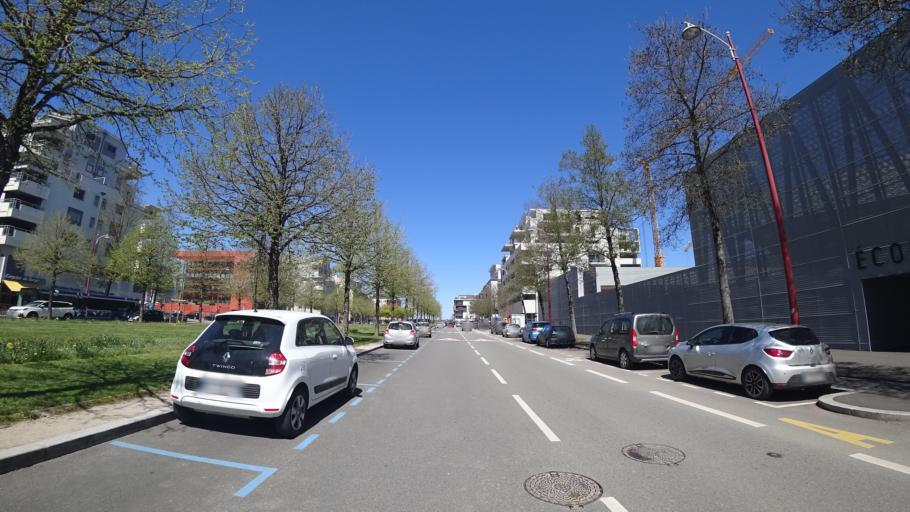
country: FR
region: Midi-Pyrenees
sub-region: Departement de l'Aveyron
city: Olemps
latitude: 44.3593
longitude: 2.5569
